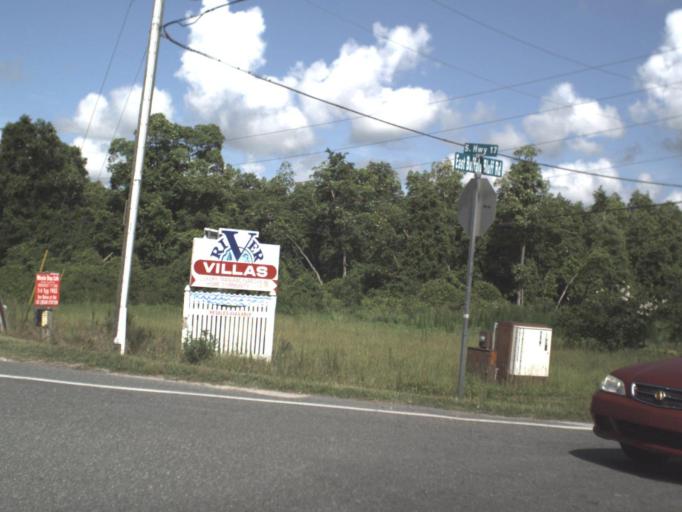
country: US
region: Florida
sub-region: Putnam County
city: Palatka
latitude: 29.5638
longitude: -81.6565
